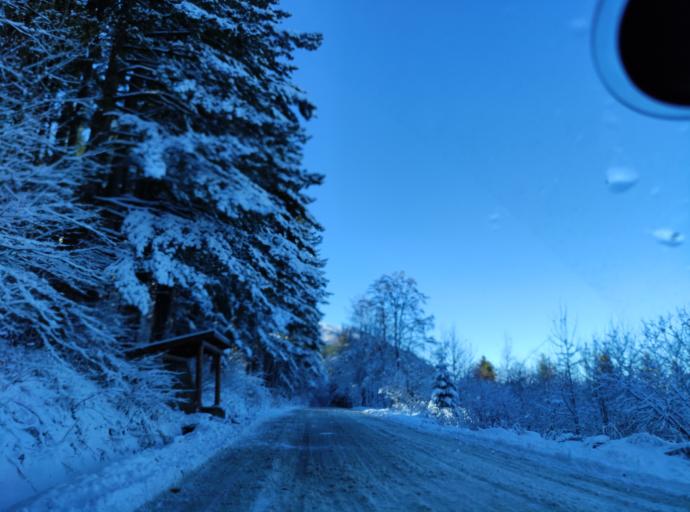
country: BG
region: Sofia-Capital
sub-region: Stolichna Obshtina
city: Sofia
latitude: 42.5946
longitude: 23.3112
